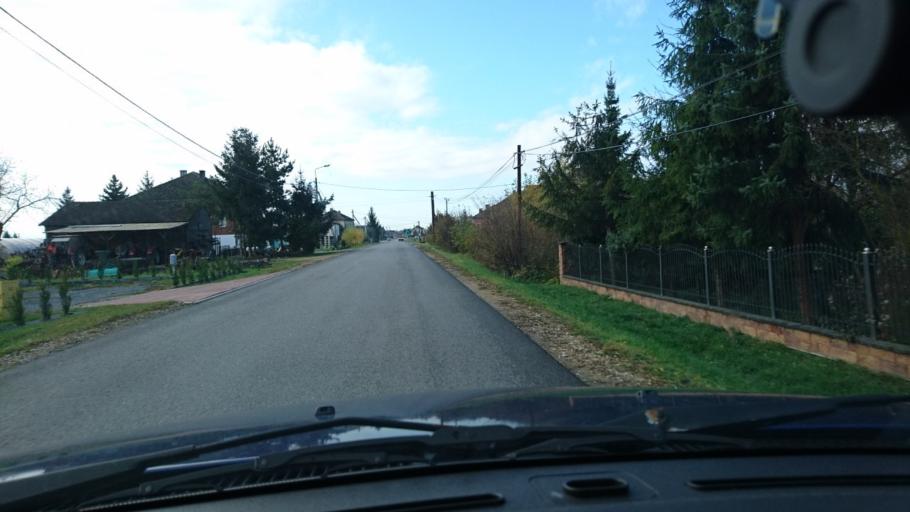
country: PL
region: Lesser Poland Voivodeship
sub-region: Powiat oswiecimski
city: Nowa Wies
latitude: 49.9399
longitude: 19.2161
